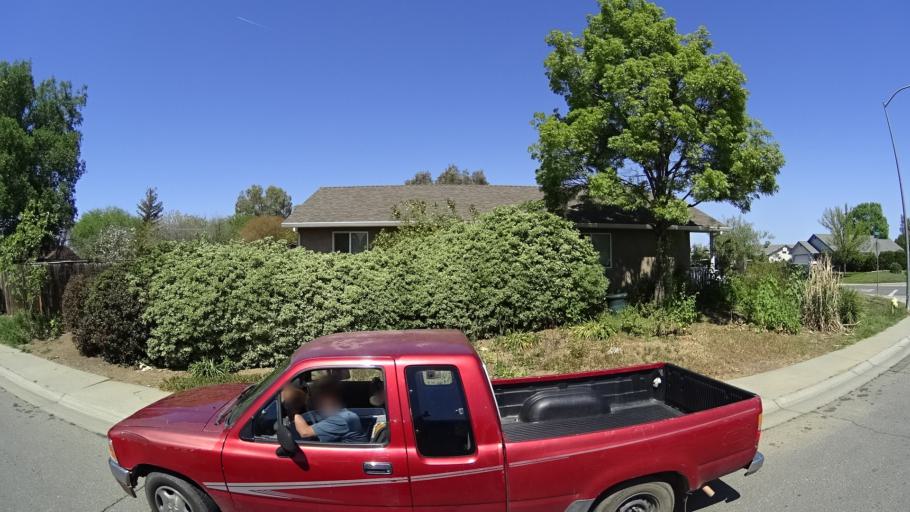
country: US
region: California
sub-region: Glenn County
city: Willows
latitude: 39.5288
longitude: -122.2103
